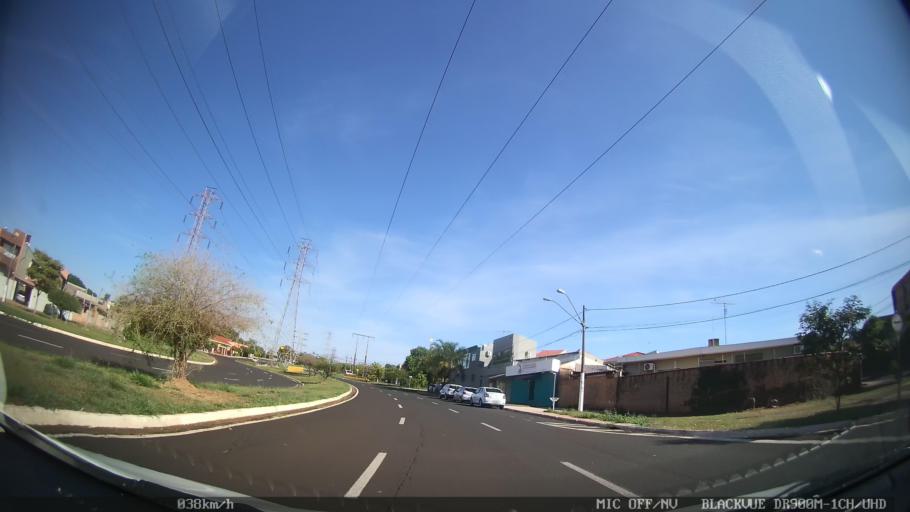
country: BR
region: Sao Paulo
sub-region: Ribeirao Preto
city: Ribeirao Preto
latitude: -21.1828
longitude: -47.7832
